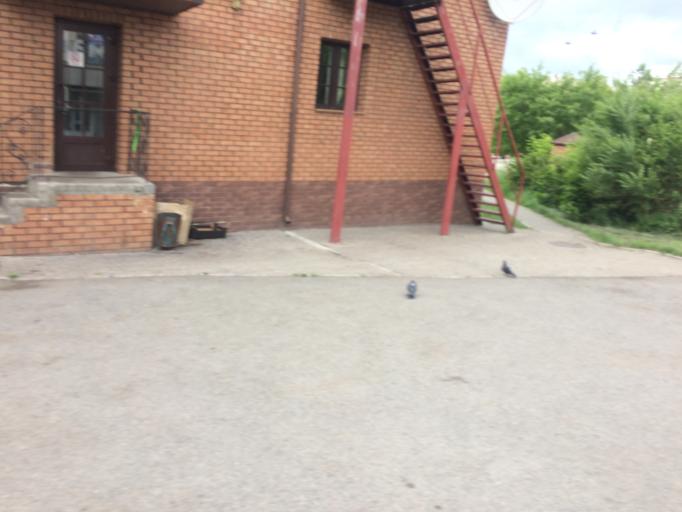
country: RU
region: Chelyabinsk
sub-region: Gorod Magnitogorsk
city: Magnitogorsk
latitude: 53.4110
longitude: 58.9802
